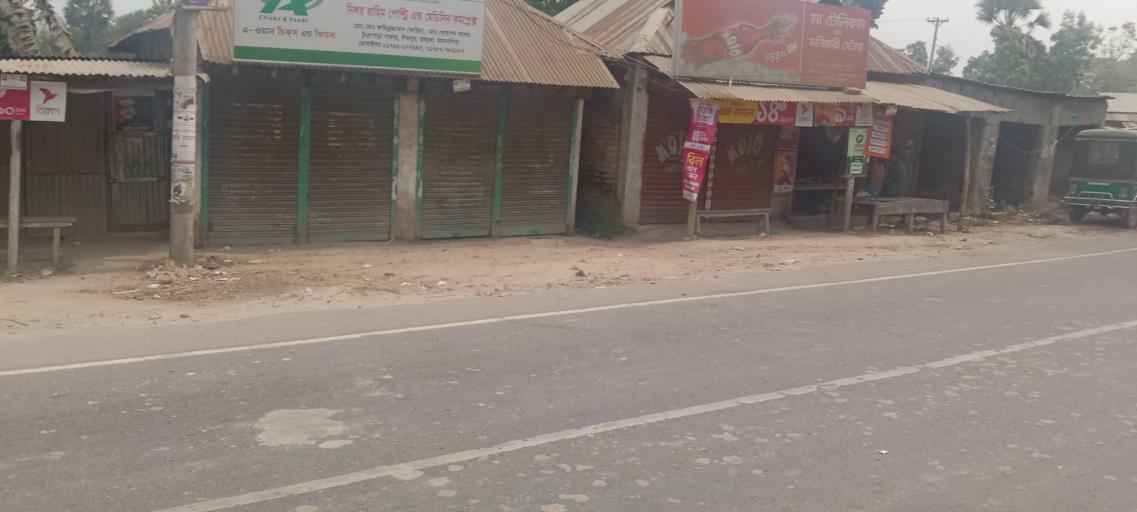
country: BD
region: Dhaka
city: Gafargaon
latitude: 24.4308
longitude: 90.4584
